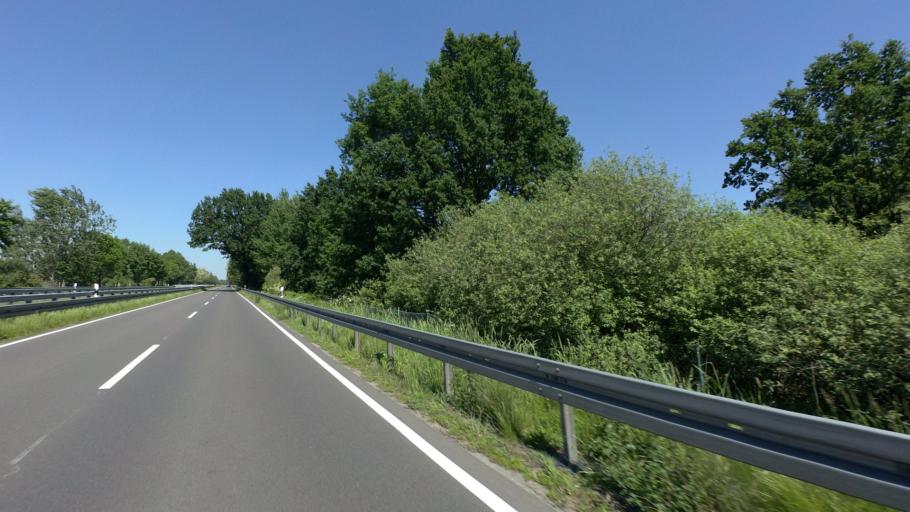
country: DE
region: Brandenburg
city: Peitz
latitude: 51.8301
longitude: 14.3872
